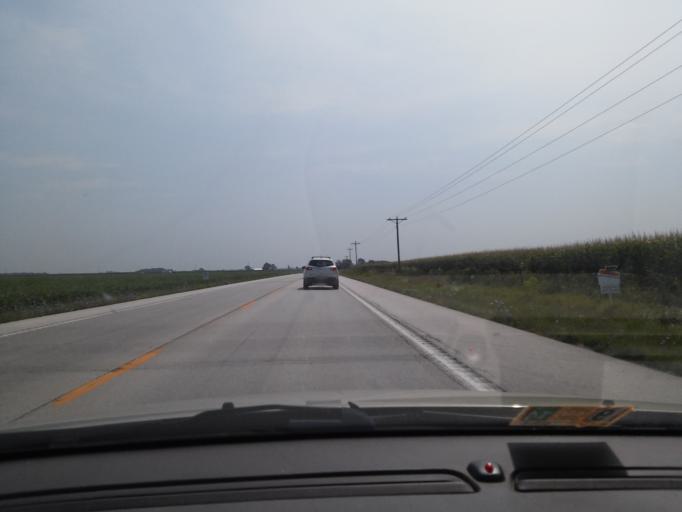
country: US
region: Missouri
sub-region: Audrain County
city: Mexico
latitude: 39.1640
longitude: -91.7310
